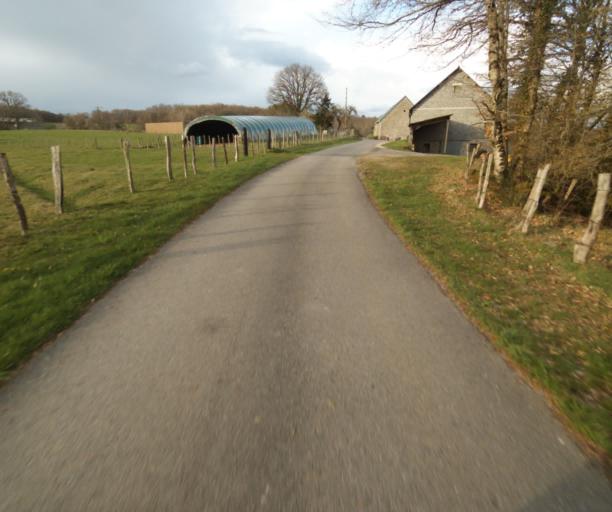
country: FR
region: Limousin
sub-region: Departement de la Correze
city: Argentat
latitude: 45.2259
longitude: 1.9517
